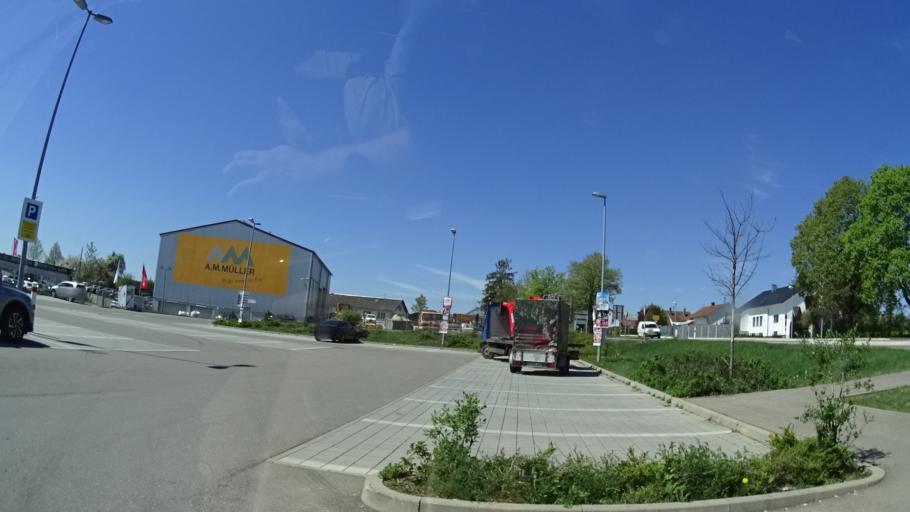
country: DE
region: Baden-Wuerttemberg
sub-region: Freiburg Region
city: Zimmern ob Rottweil
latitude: 48.1655
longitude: 8.6033
